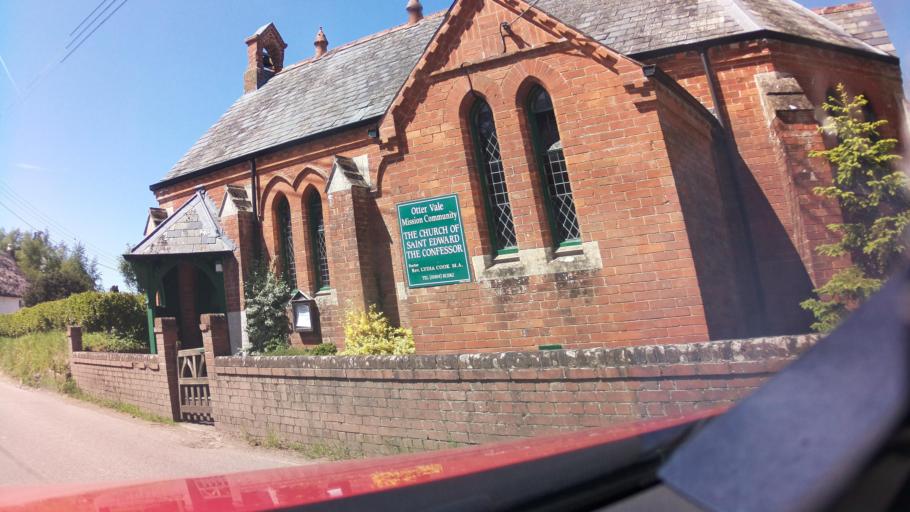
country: GB
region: England
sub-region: Devon
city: Ottery St Mary
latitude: 50.7355
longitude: -3.2757
